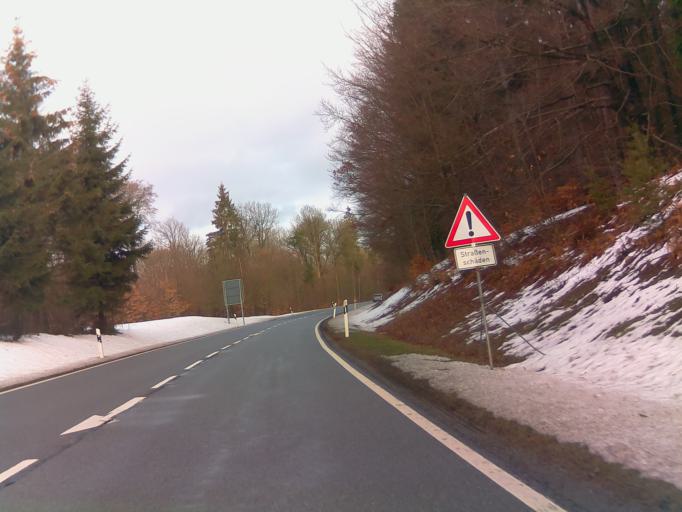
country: DE
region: Baden-Wuerttemberg
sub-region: Karlsruhe Region
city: Fahrenbach
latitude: 49.4865
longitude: 9.1475
